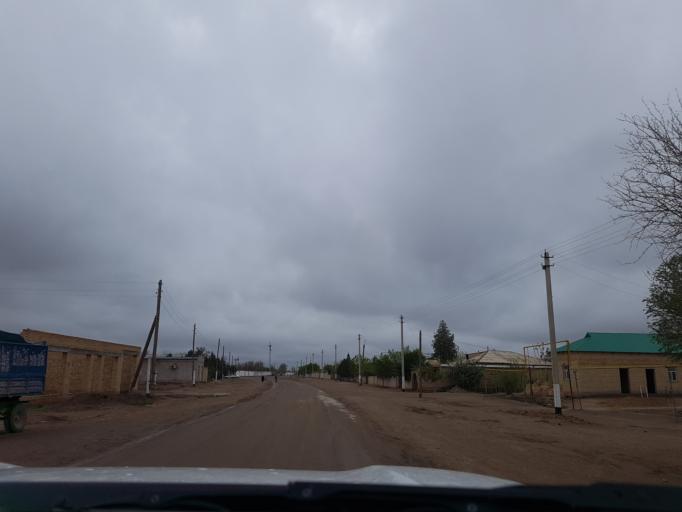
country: TM
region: Lebap
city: Sayat
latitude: 38.4521
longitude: 64.3796
